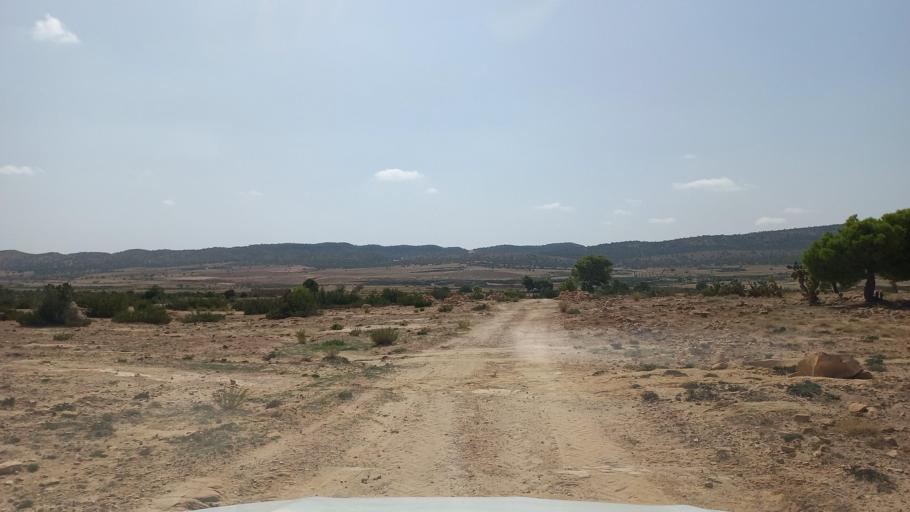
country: TN
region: Al Qasrayn
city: Sbiba
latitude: 35.3978
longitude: 8.9586
